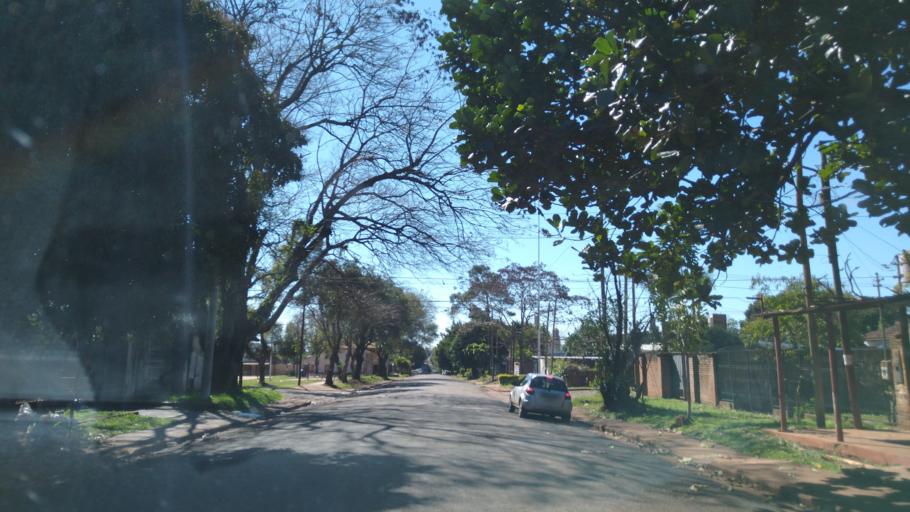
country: AR
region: Misiones
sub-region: Departamento de Capital
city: Posadas
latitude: -27.3995
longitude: -55.9343
